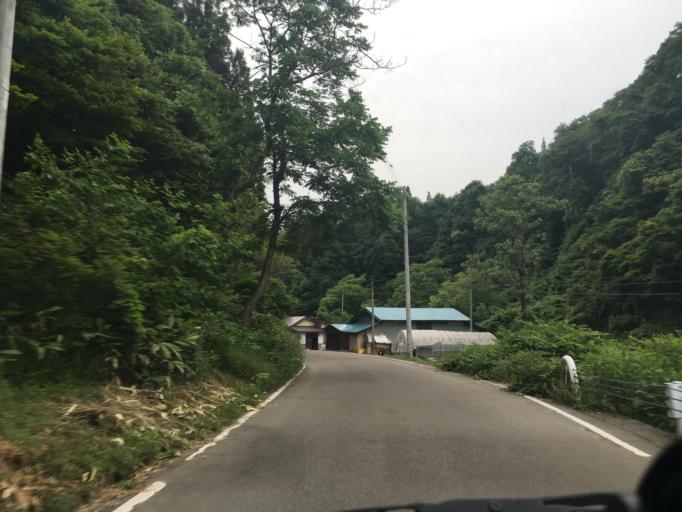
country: JP
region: Fukushima
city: Kitakata
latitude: 37.5171
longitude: 139.7305
